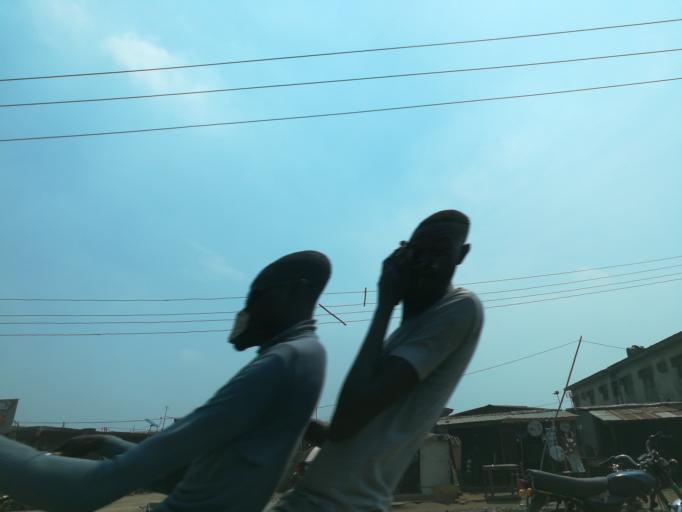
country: NG
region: Lagos
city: Ikorodu
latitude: 6.6375
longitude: 3.4817
